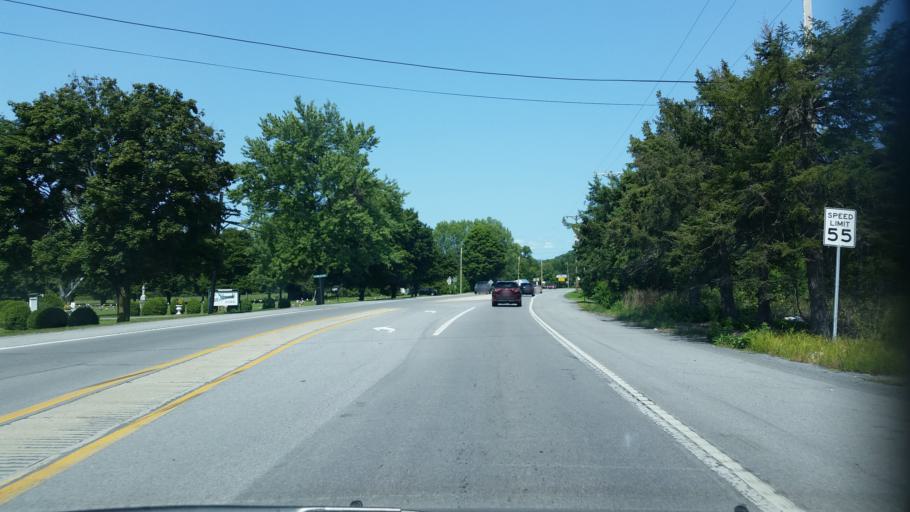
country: US
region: Pennsylvania
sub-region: Blair County
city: Bellwood
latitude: 40.6008
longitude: -78.3200
